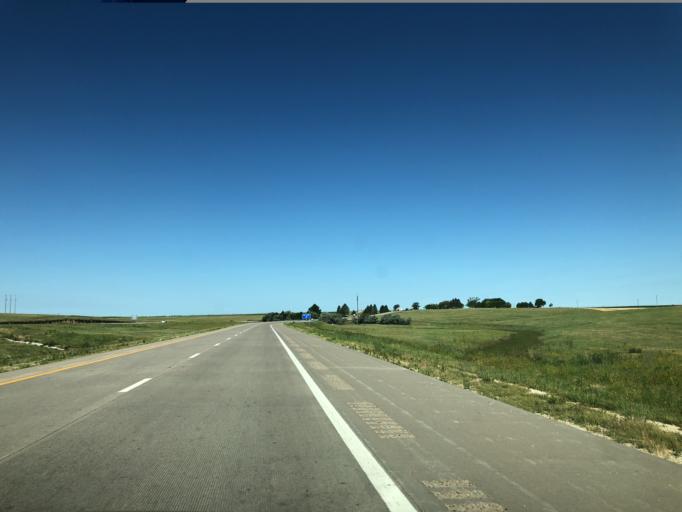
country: US
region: Kansas
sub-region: Sherman County
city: Goodland
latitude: 39.3294
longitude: -101.9063
